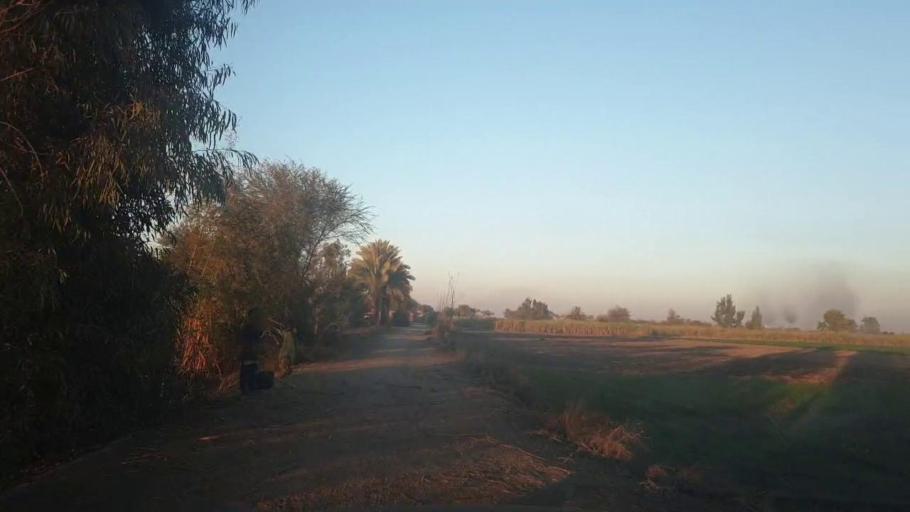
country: PK
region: Sindh
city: Ghotki
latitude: 28.0324
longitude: 69.2950
